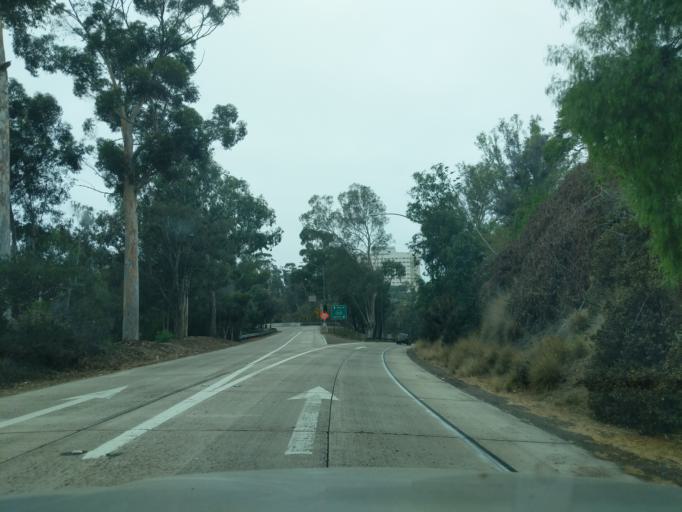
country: US
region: California
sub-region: San Diego County
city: San Diego
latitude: 32.7513
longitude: -117.1537
